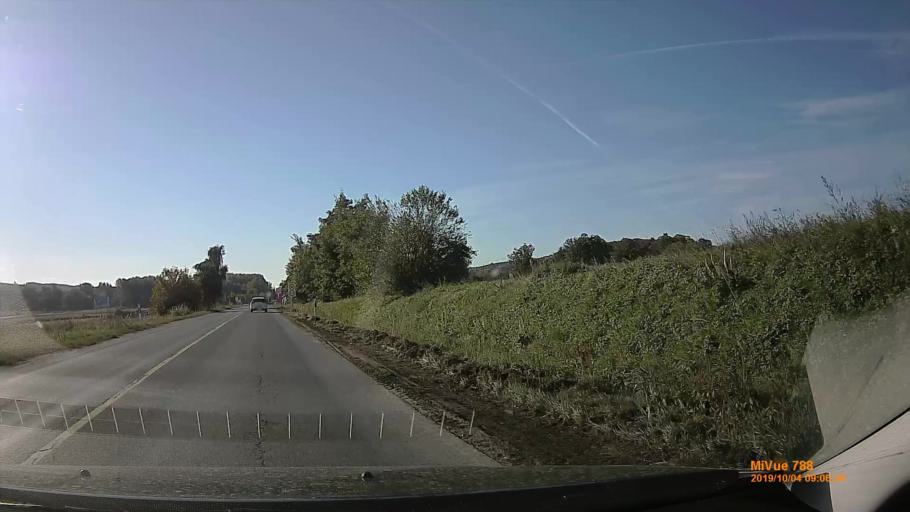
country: HU
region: Somogy
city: Karad
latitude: 46.6853
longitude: 17.7713
